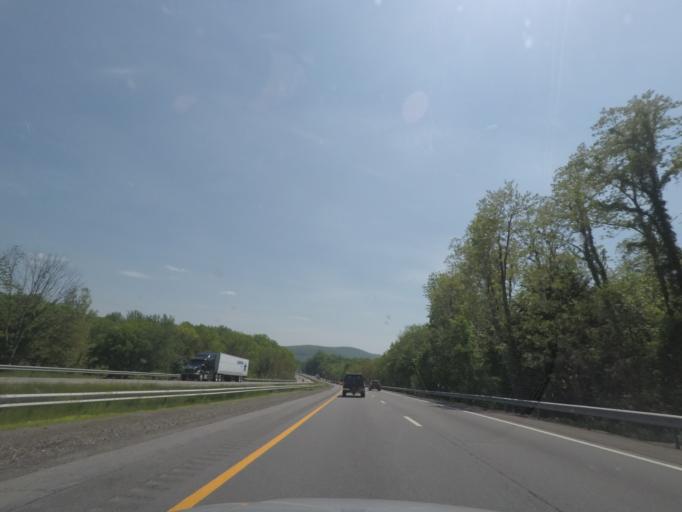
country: US
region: New York
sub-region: Orange County
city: Central Valley
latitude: 41.3414
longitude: -74.1176
